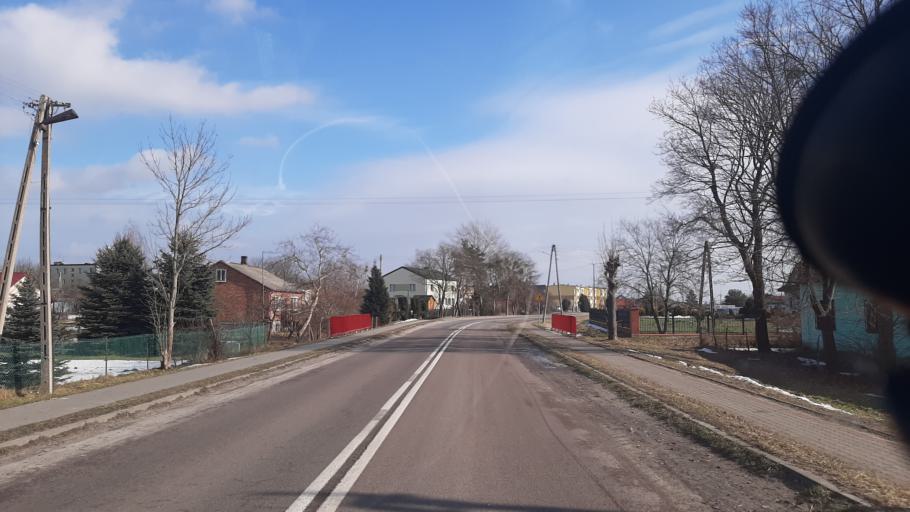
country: PL
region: Lublin Voivodeship
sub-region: Powiat wlodawski
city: Hansk
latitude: 51.4799
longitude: 23.2963
